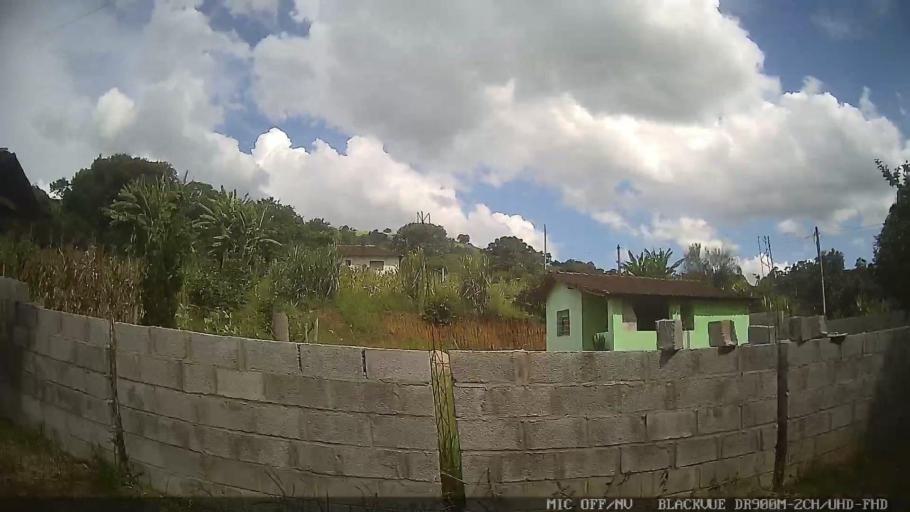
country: BR
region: Minas Gerais
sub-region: Extrema
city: Extrema
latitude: -22.8376
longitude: -46.2462
